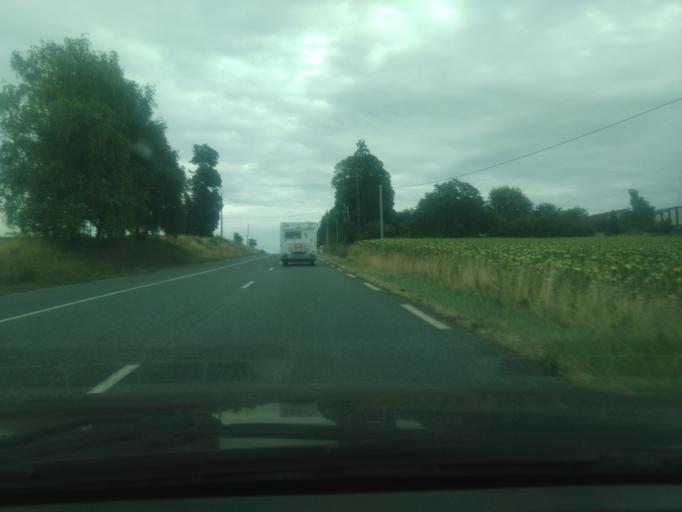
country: FR
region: Auvergne
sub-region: Departement de l'Allier
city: Ainay-le-Chateau
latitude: 46.7578
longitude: 2.7929
